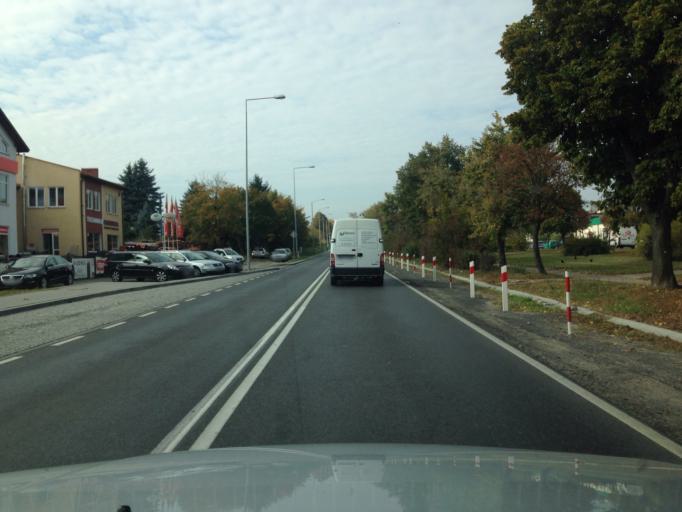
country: PL
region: Kujawsko-Pomorskie
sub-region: Powiat brodnicki
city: Brodnica
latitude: 53.2604
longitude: 19.3843
